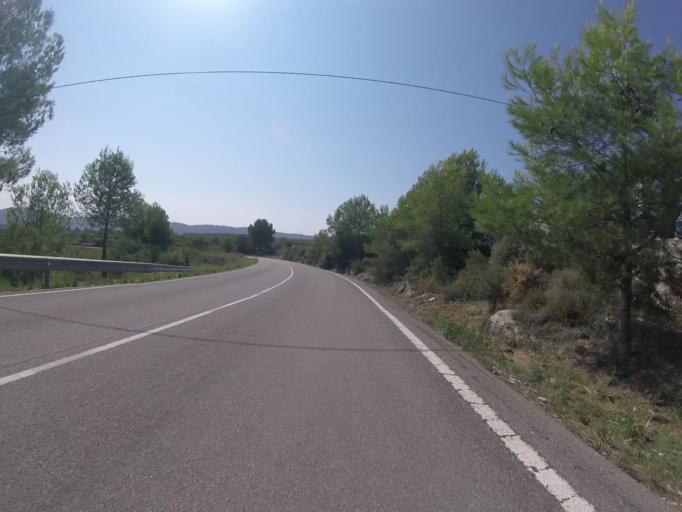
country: ES
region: Valencia
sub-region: Provincia de Castello
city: Adzaneta
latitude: 40.2374
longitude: -0.1891
